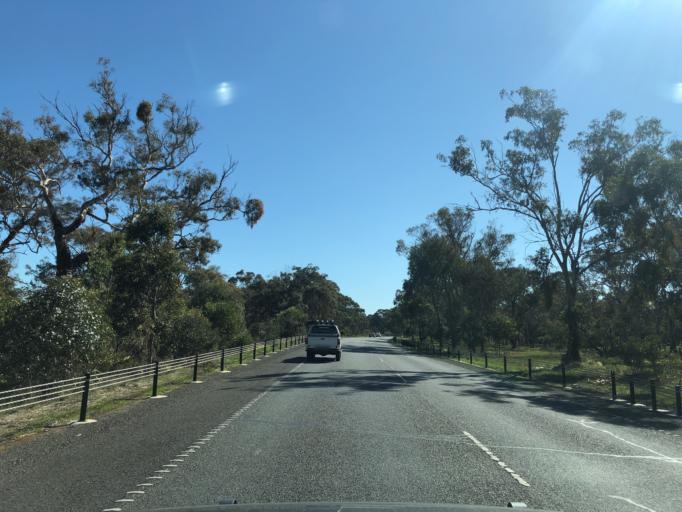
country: AU
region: Victoria
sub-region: Melton
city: Kurunjang
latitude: -37.6159
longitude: 144.6175
